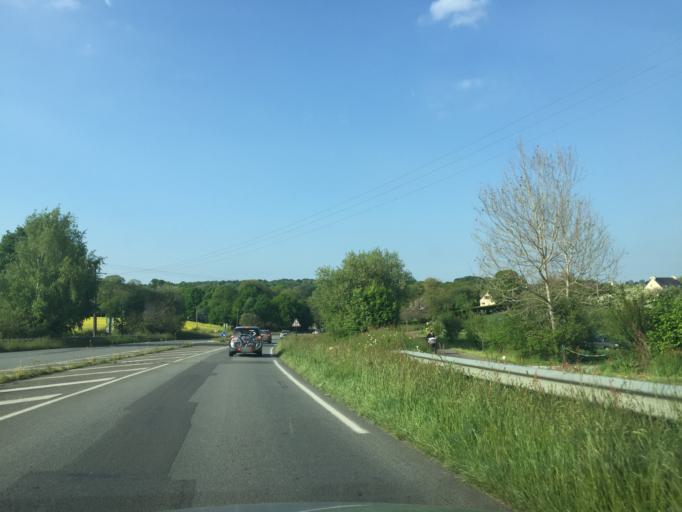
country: FR
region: Brittany
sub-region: Departement des Cotes-d'Armor
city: Trelivan
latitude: 48.3871
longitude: -2.0876
